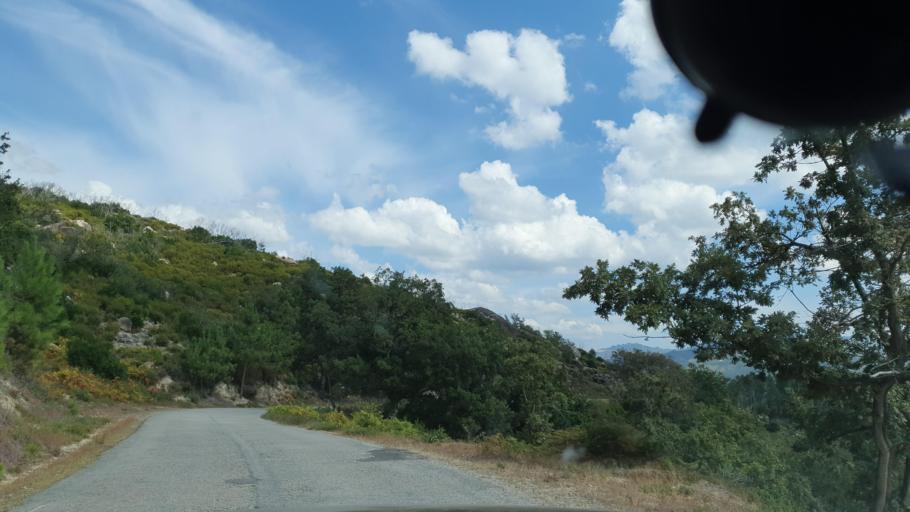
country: PT
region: Braga
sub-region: Vieira do Minho
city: Vieira do Minho
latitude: 41.7008
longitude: -8.0608
